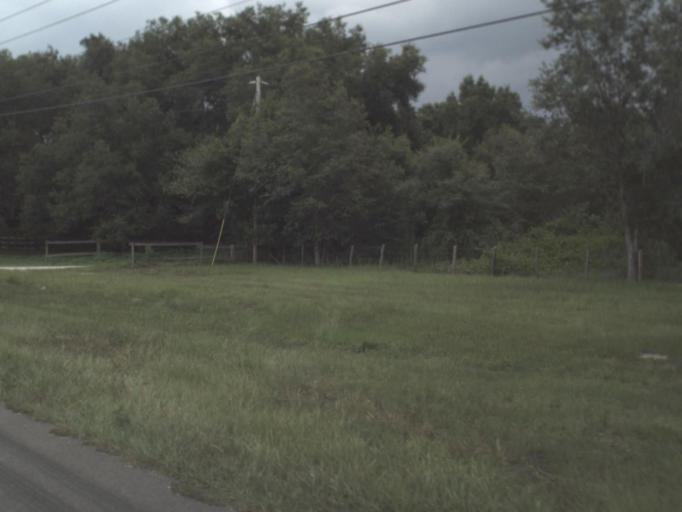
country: US
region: Florida
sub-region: Pasco County
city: Shady Hills
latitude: 28.3860
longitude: -82.4891
